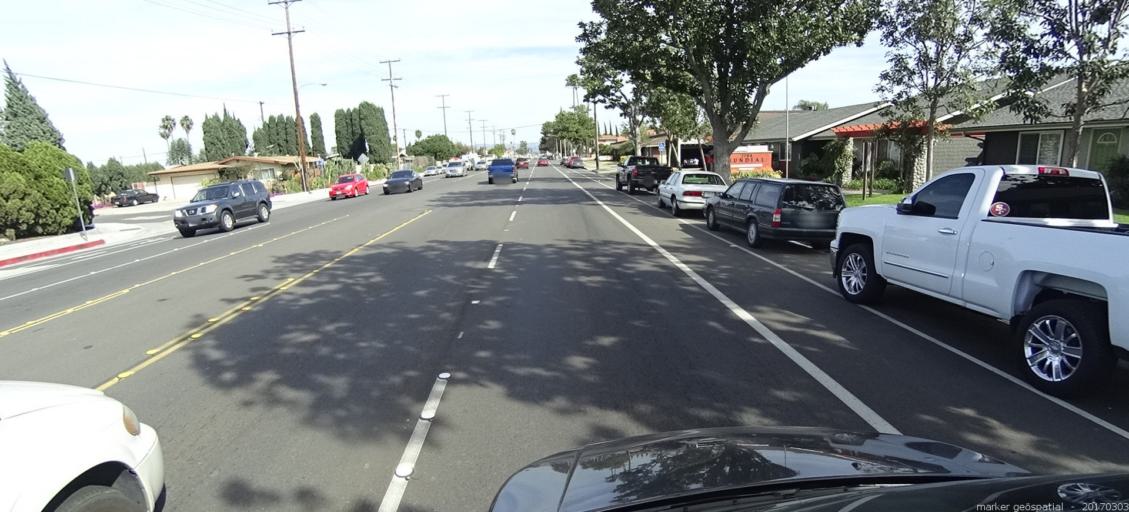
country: US
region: California
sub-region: Orange County
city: Stanton
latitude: 33.8175
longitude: -117.9801
